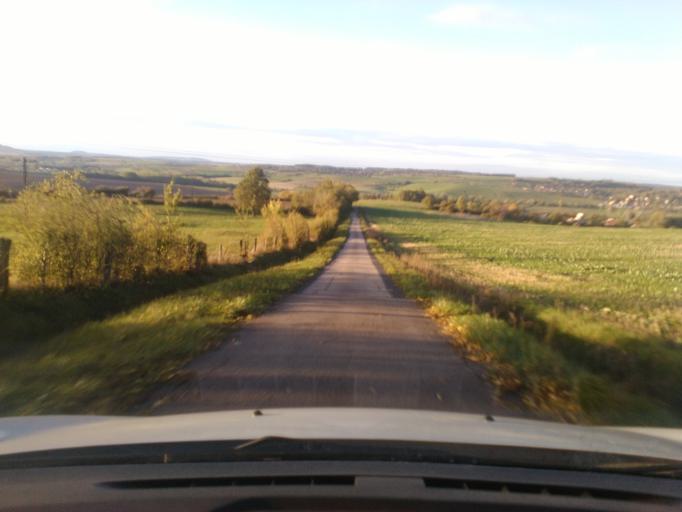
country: FR
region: Lorraine
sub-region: Departement des Vosges
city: Charmes
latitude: 48.3399
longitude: 6.2539
